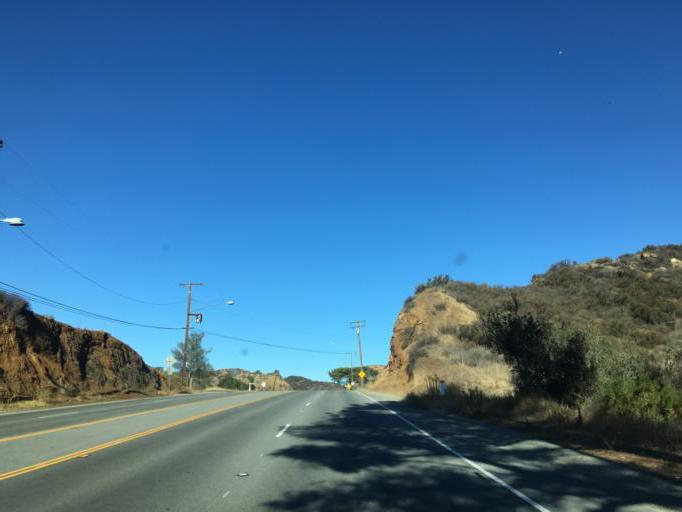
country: US
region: California
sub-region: Los Angeles County
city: Agoura Hills
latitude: 34.1301
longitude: -118.7690
